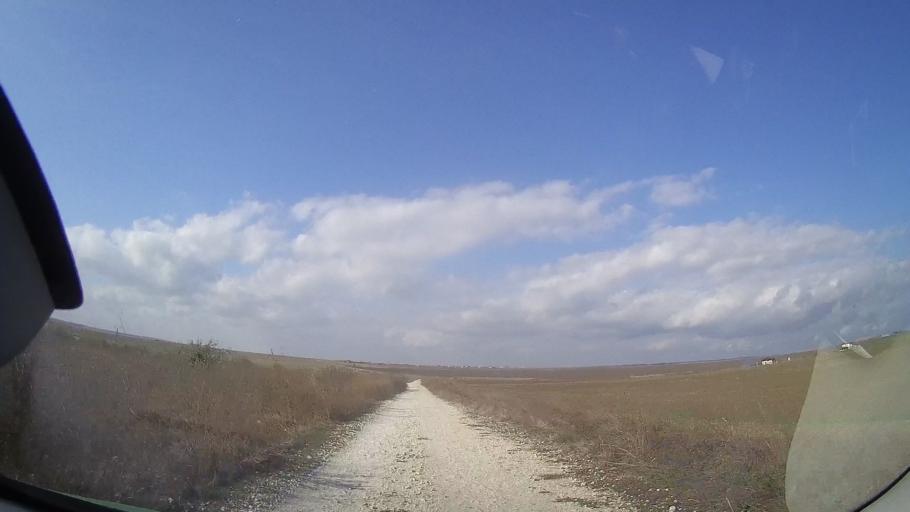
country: RO
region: Constanta
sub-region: Comuna Douazeci si Trei August
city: Douazeci si Trei August
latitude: 43.9058
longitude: 28.6146
